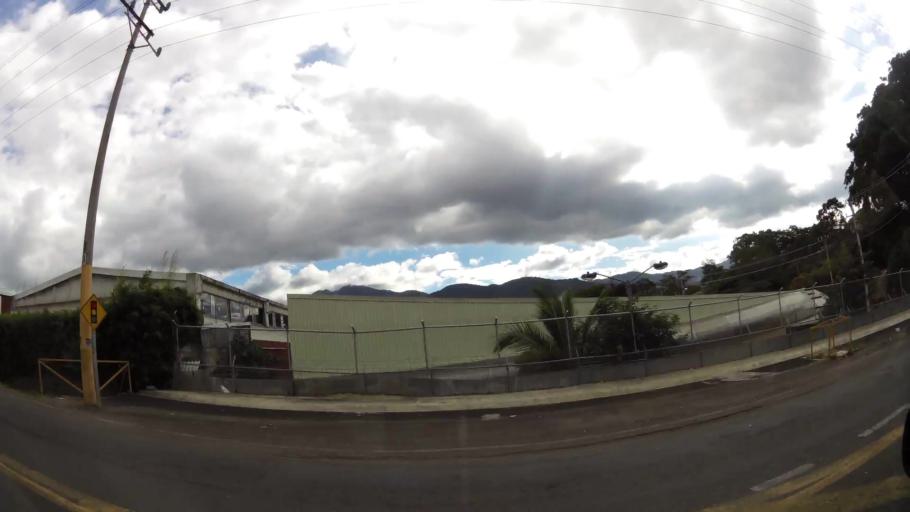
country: CR
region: San Jose
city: San Rafael
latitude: 9.9489
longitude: -84.1411
